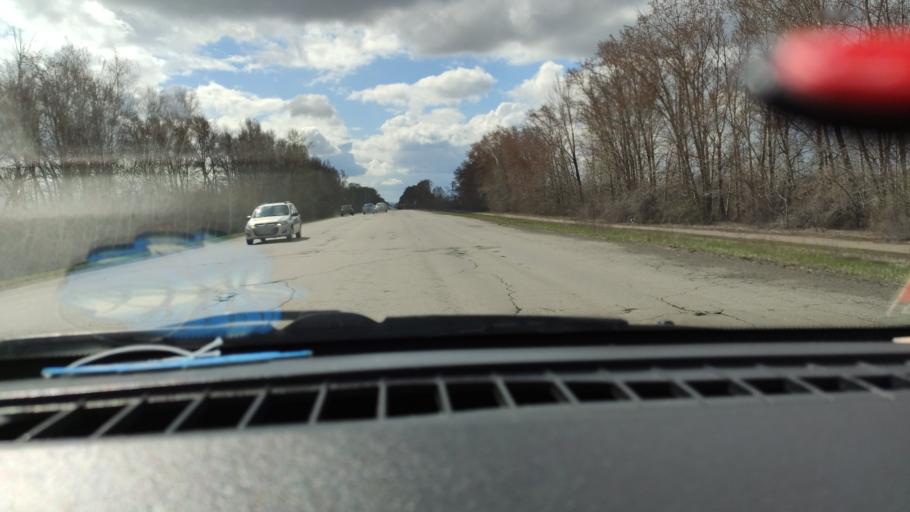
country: RU
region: Samara
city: Tol'yatti
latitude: 53.6318
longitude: 49.4176
